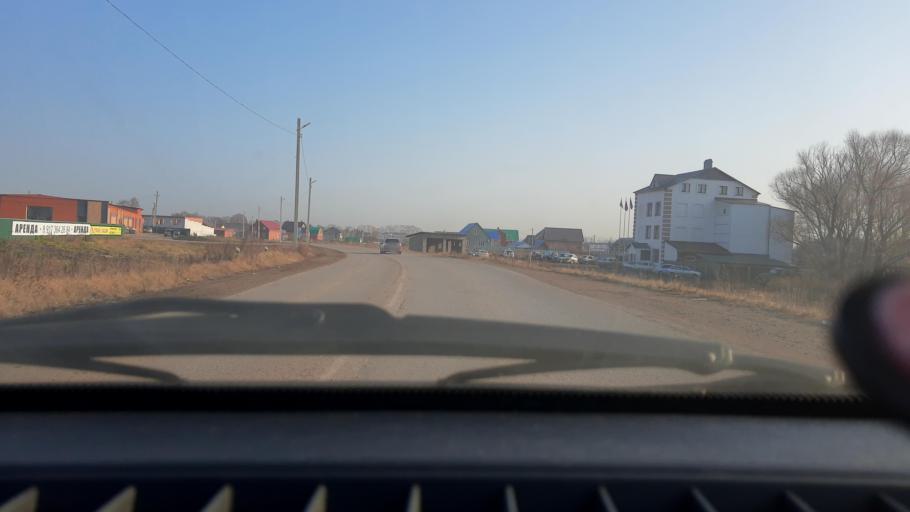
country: RU
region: Bashkortostan
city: Mikhaylovka
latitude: 54.8003
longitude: 55.8777
